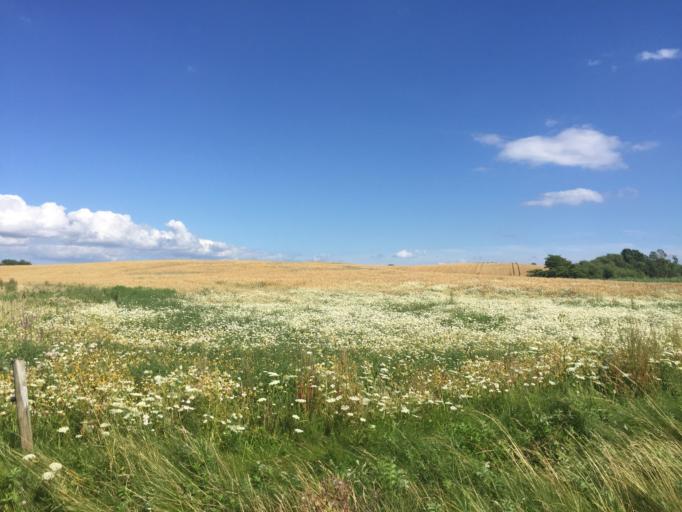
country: DK
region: South Denmark
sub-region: Faaborg-Midtfyn Kommune
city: Faaborg
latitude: 55.0674
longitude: 10.2353
